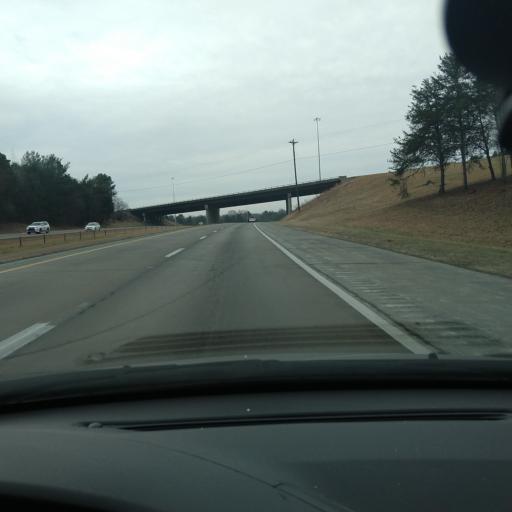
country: US
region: North Carolina
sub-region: Davidson County
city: Midway
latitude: 35.9719
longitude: -80.2303
